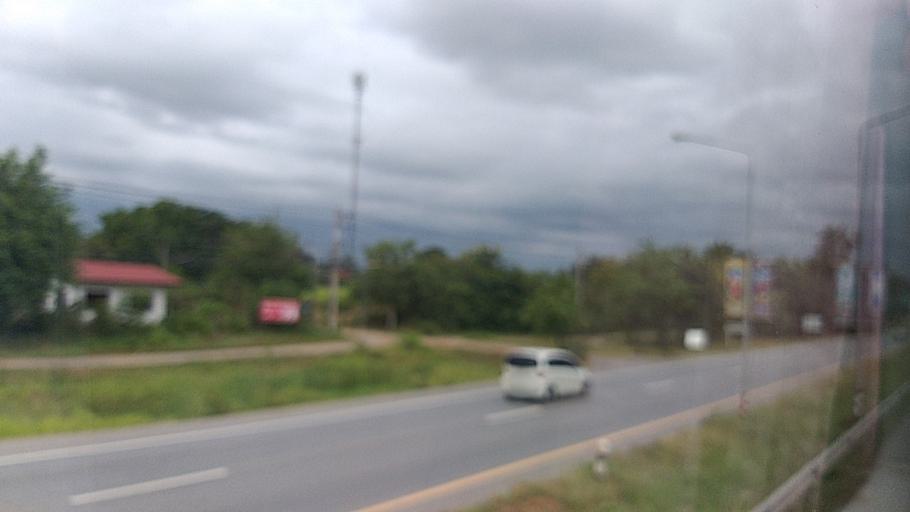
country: TH
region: Khon Kaen
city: Non Sila
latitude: 15.9626
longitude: 102.6903
